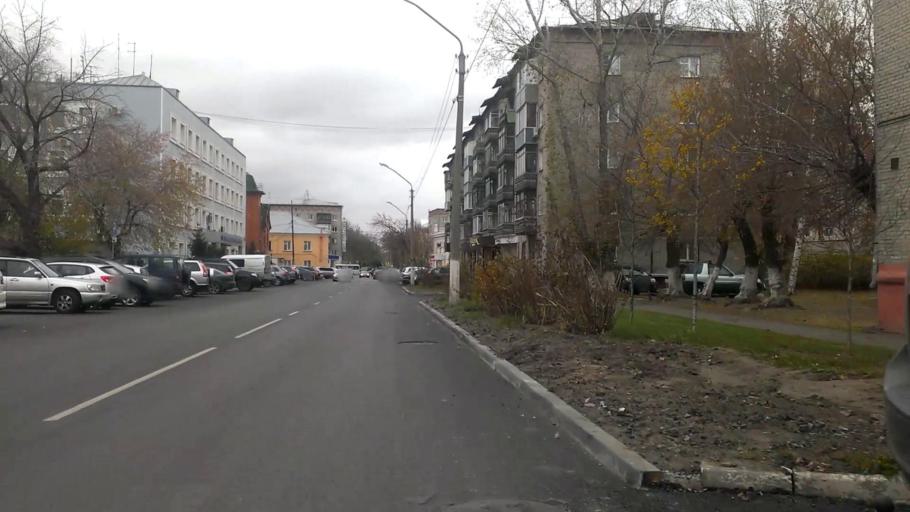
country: RU
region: Altai Krai
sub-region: Gorod Barnaulskiy
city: Barnaul
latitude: 53.3521
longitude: 83.7686
